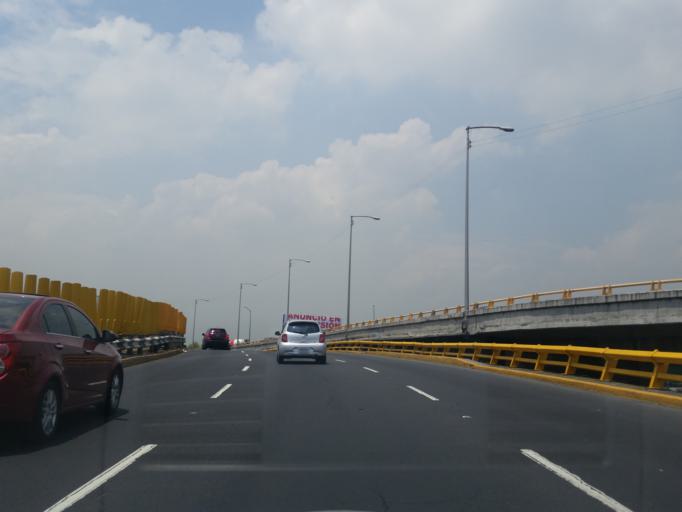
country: MX
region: Mexico City
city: Cuauhtemoc
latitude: 19.4641
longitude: -99.1582
